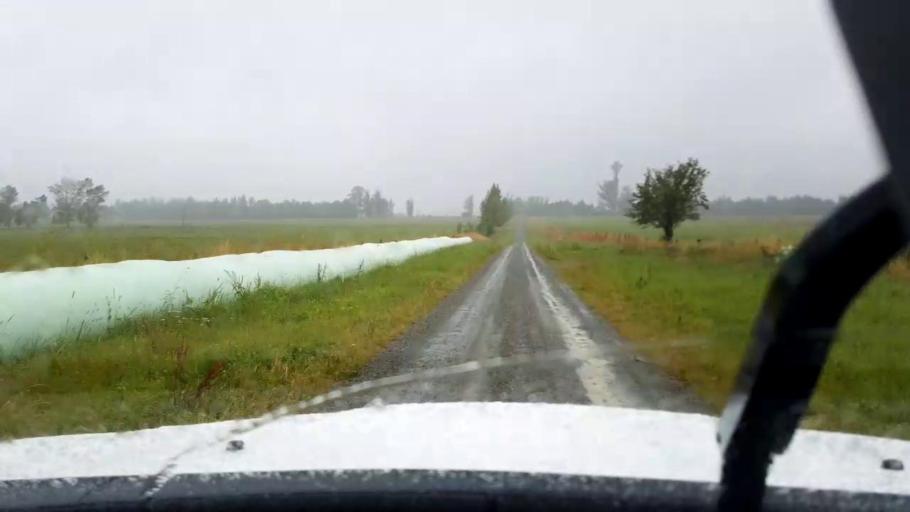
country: NZ
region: Canterbury
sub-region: Timaru District
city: Pleasant Point
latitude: -44.1976
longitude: 171.0910
